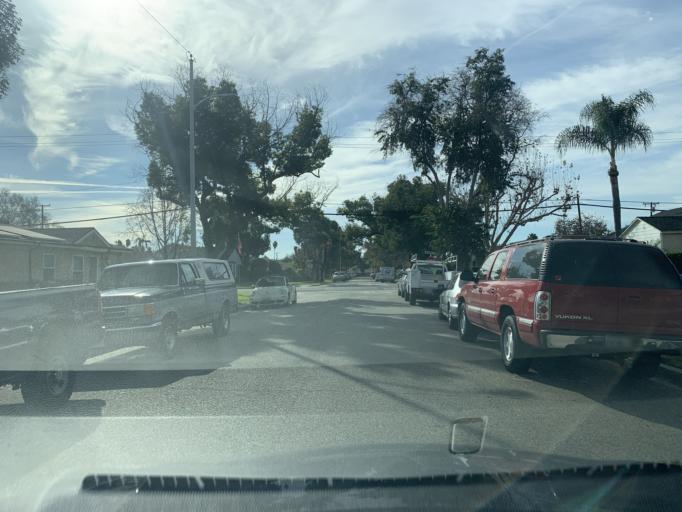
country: US
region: California
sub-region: Los Angeles County
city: West Covina
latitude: 34.0760
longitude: -117.9331
